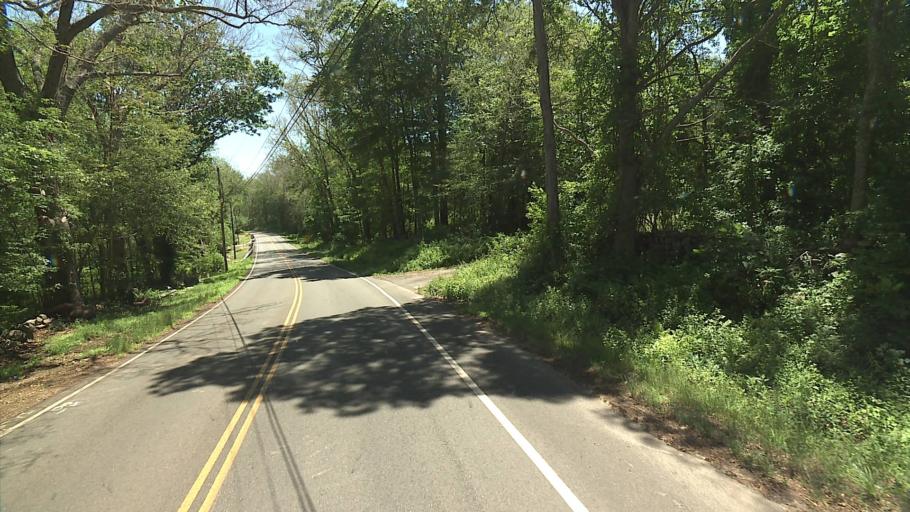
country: US
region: Connecticut
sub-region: New London County
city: Old Mystic
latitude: 41.3836
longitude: -71.9398
